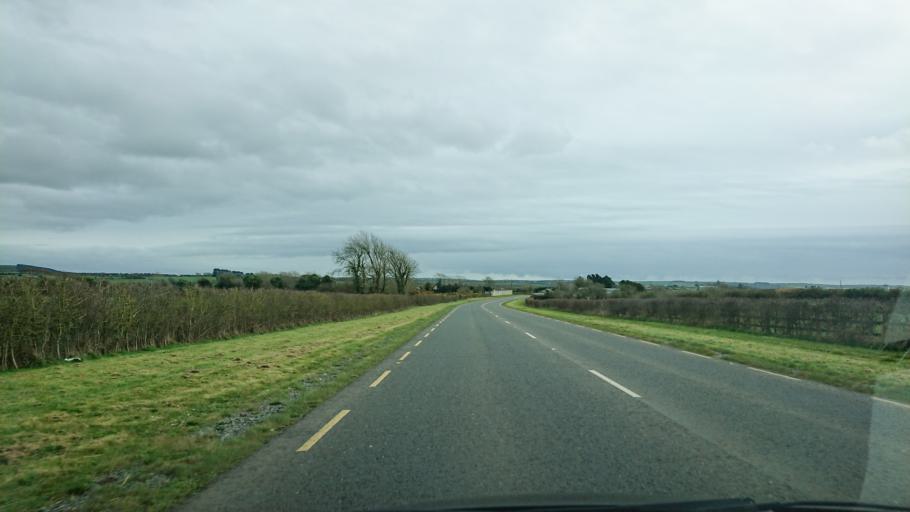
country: IE
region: Munster
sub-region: Waterford
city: Waterford
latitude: 52.1982
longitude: -7.0788
